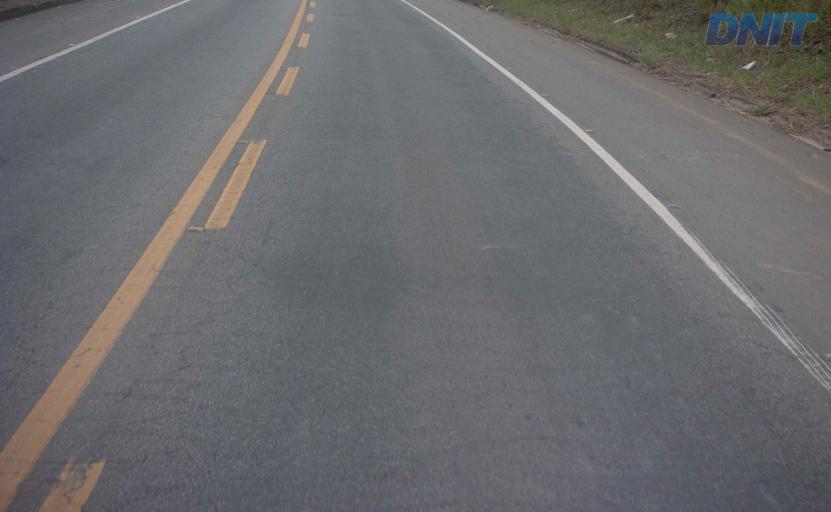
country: BR
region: Minas Gerais
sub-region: Coronel Fabriciano
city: Coronel Fabriciano
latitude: -19.5231
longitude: -42.5814
